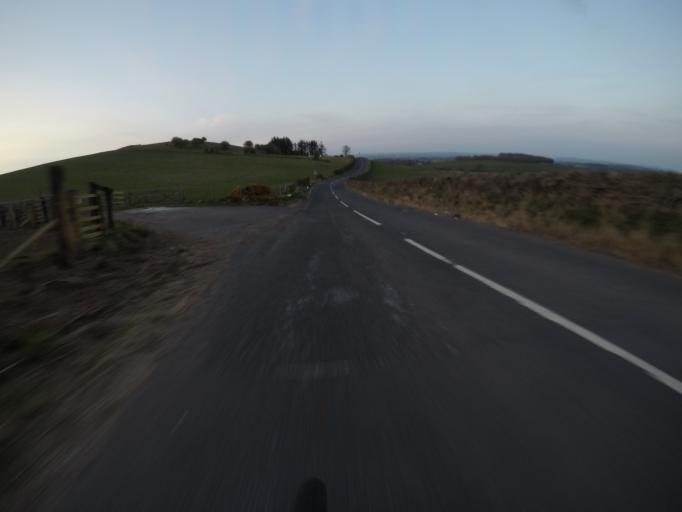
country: GB
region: Scotland
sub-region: South Ayrshire
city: Dundonald
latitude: 55.5632
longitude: -4.6048
